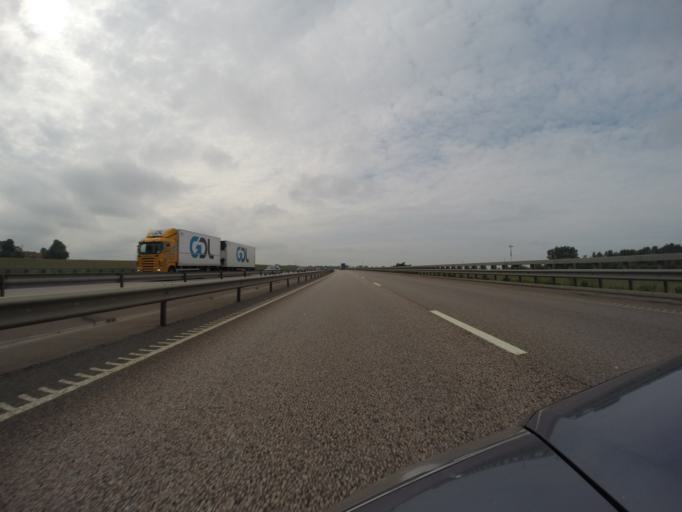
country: SE
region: Skane
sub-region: Helsingborg
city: Gantofta
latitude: 55.9875
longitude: 12.7810
